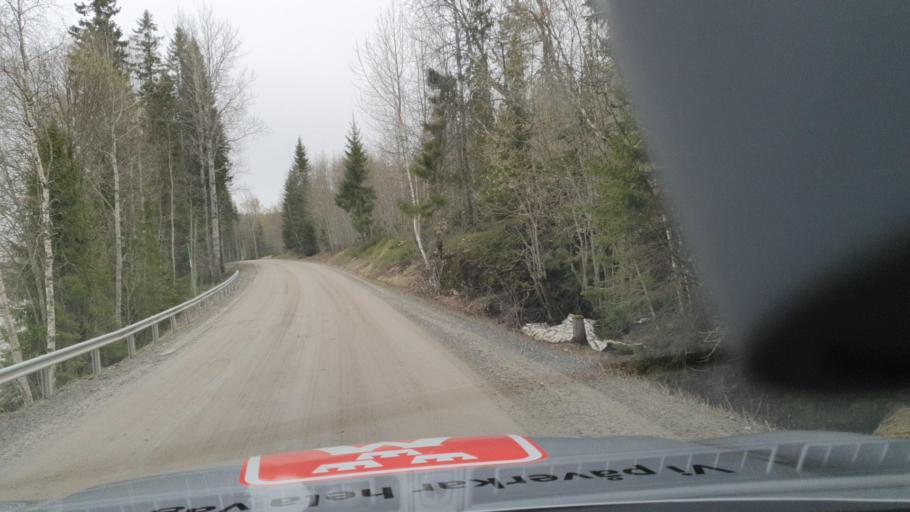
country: SE
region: Vaesternorrland
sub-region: OErnskoeldsviks Kommun
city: Husum
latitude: 63.6353
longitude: 19.0587
